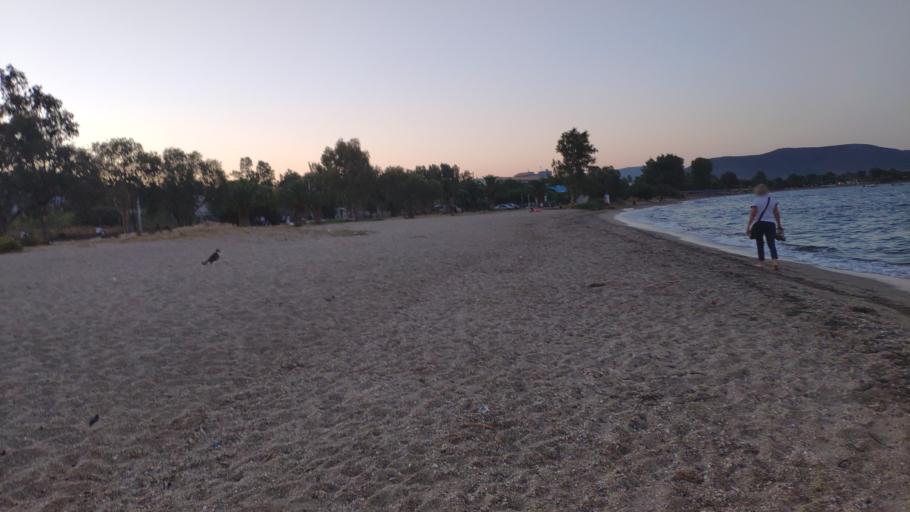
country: GR
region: Attica
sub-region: Nomarchia Anatolikis Attikis
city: Nea Makri
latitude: 38.1013
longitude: 23.9808
